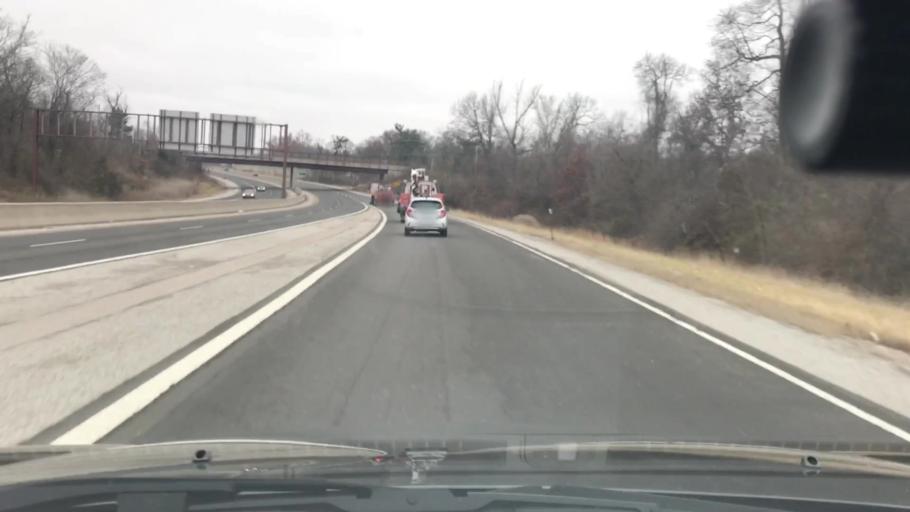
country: US
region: Illinois
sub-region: Madison County
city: Rosewood Heights
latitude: 38.8990
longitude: -90.0659
